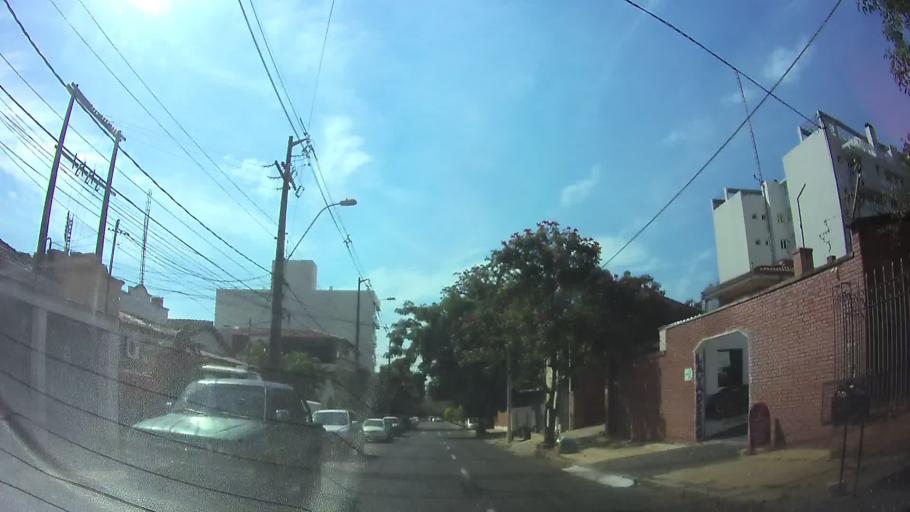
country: PY
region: Asuncion
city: Asuncion
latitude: -25.2925
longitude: -57.6073
